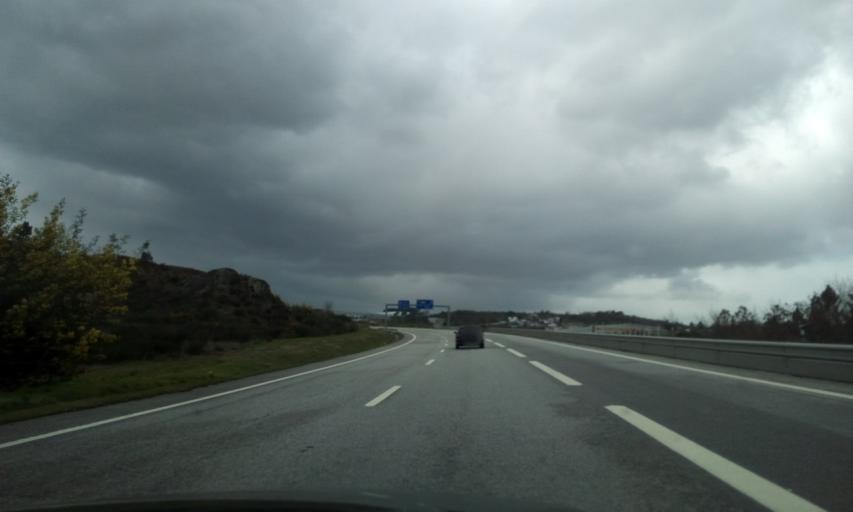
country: PT
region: Viseu
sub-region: Viseu
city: Rio de Loba
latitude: 40.6335
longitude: -7.8286
